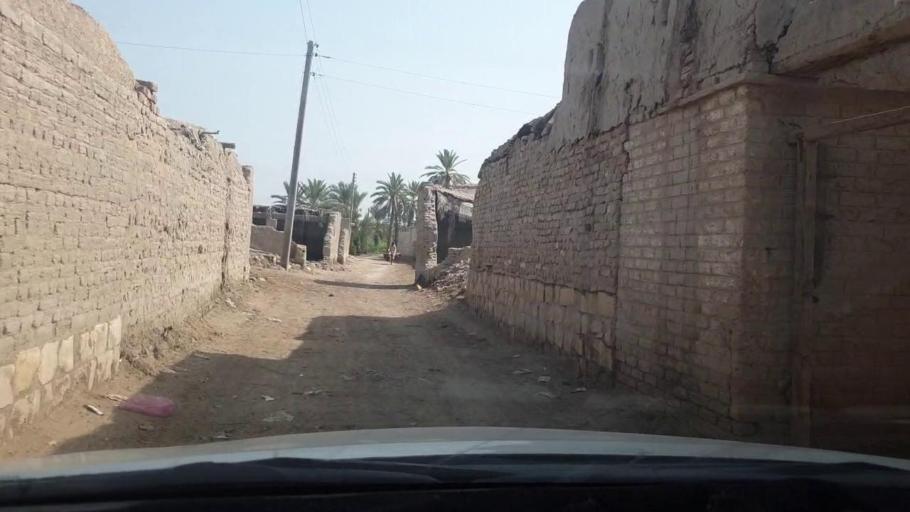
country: PK
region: Sindh
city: Rohri
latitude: 27.6040
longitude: 68.8909
